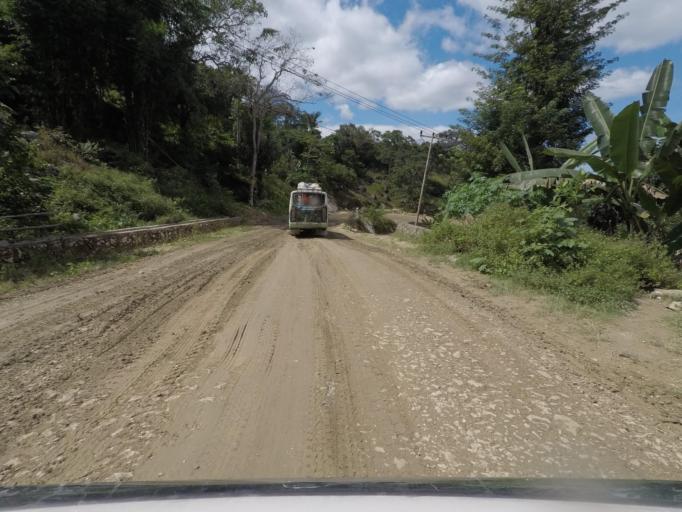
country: TL
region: Baucau
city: Venilale
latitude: -8.7326
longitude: 126.3688
